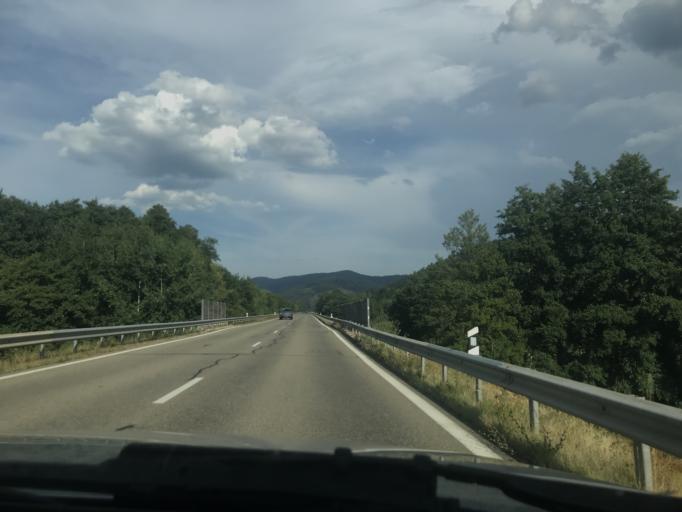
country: FR
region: Lorraine
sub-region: Departement des Vosges
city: Ban-de-Laveline
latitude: 48.2916
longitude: 7.0910
